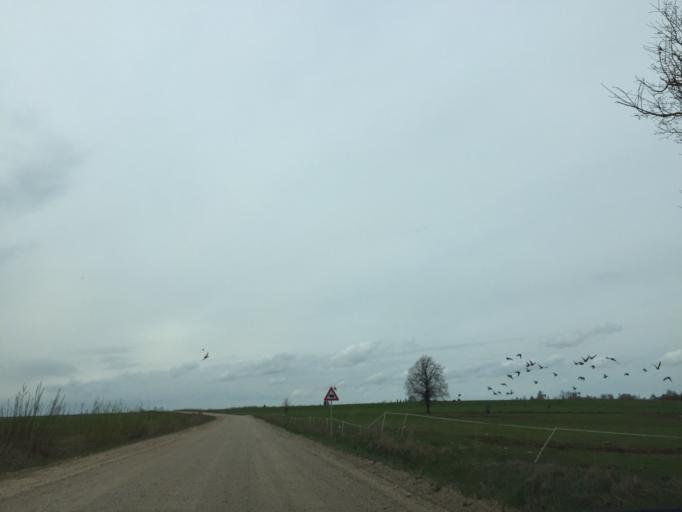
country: LV
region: Priekuli
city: Priekuli
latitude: 57.3408
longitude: 25.3605
